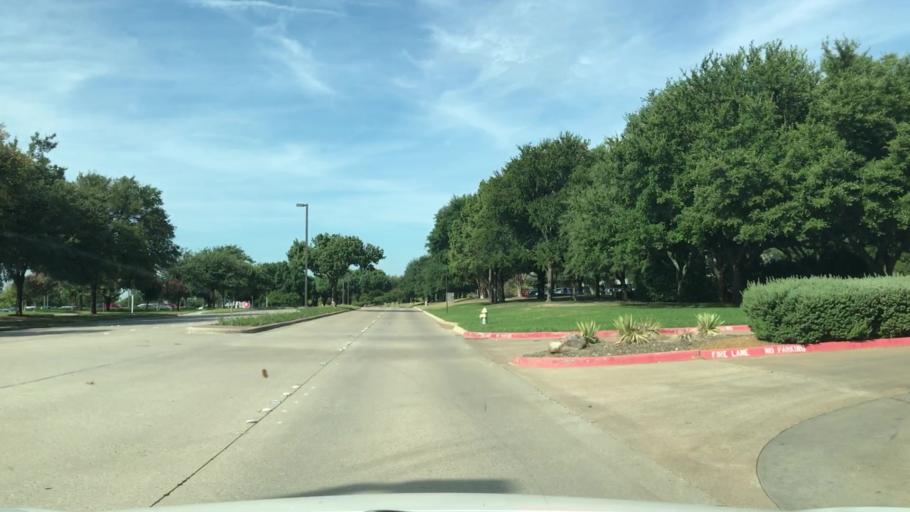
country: US
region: Texas
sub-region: Denton County
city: The Colony
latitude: 33.0769
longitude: -96.8350
